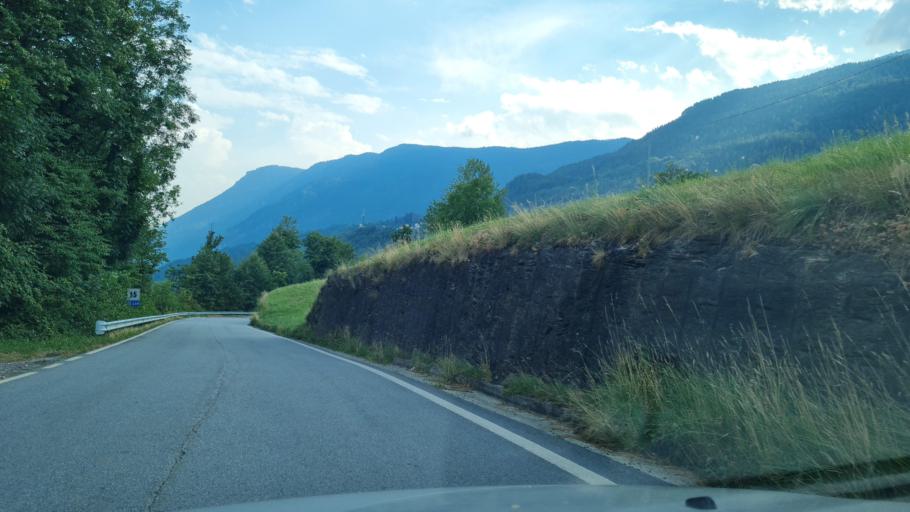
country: IT
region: Piedmont
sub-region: Provincia Verbano-Cusio-Ossola
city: Baceno
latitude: 46.2577
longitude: 8.3260
